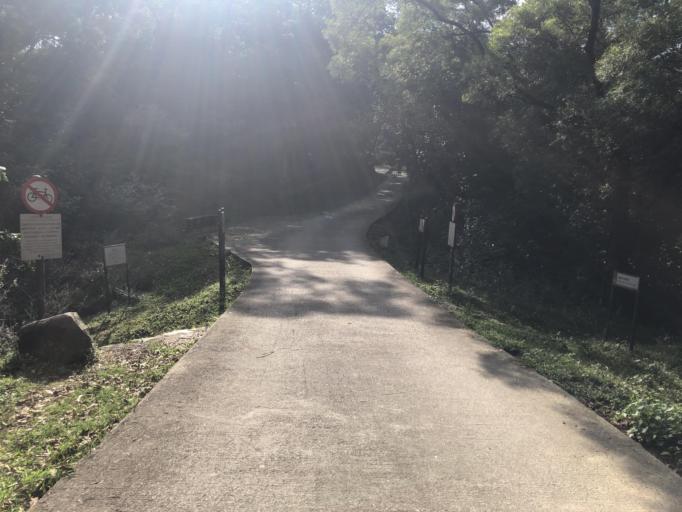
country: HK
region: Tsuen Wan
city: Tsuen Wan
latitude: 22.4005
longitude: 114.0944
